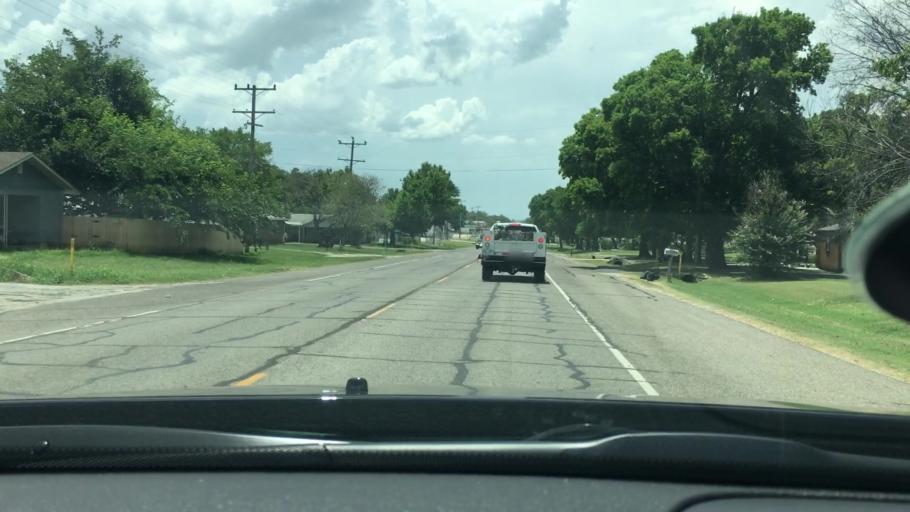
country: US
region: Oklahoma
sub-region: Love County
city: Marietta
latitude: 33.9445
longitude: -97.1263
